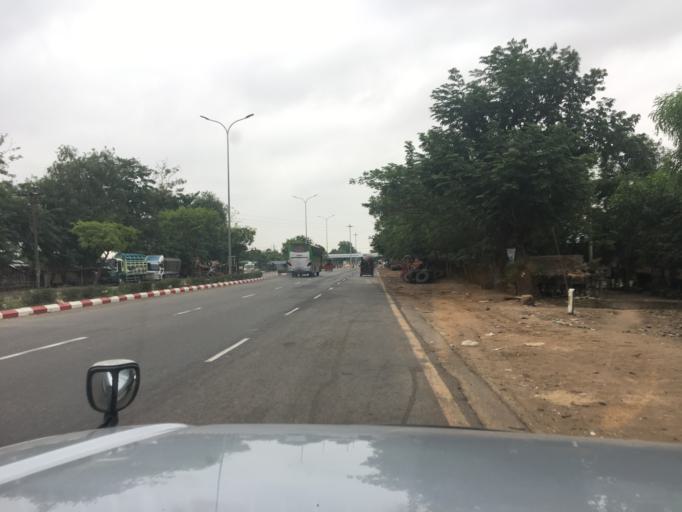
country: MM
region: Bago
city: Bago
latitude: 17.2516
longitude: 96.4678
